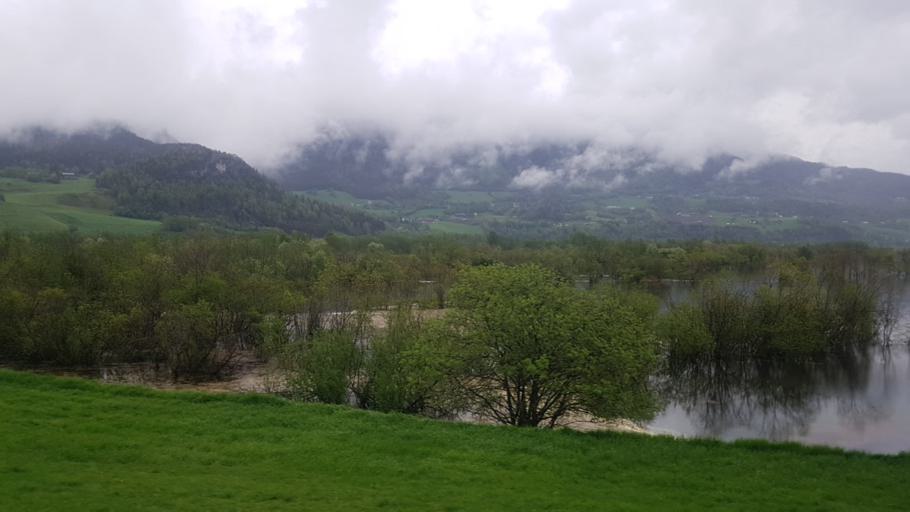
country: NO
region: Oppland
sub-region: Ringebu
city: Ringebu
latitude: 61.4583
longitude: 10.1934
